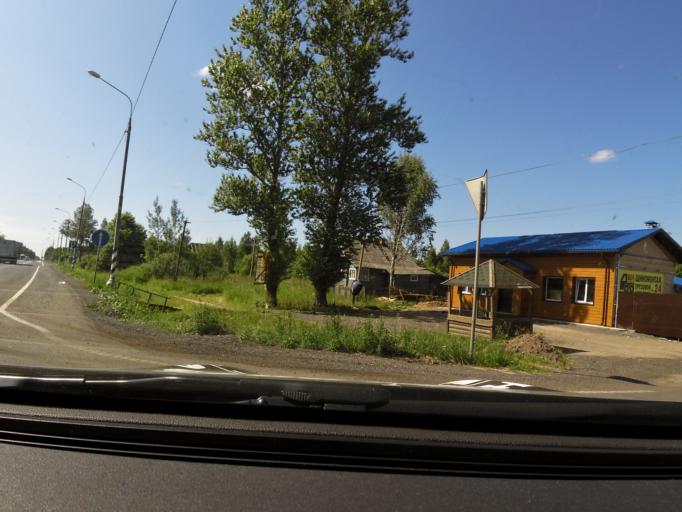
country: RU
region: Novgorod
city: Proletariy
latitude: 58.3853
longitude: 31.9815
